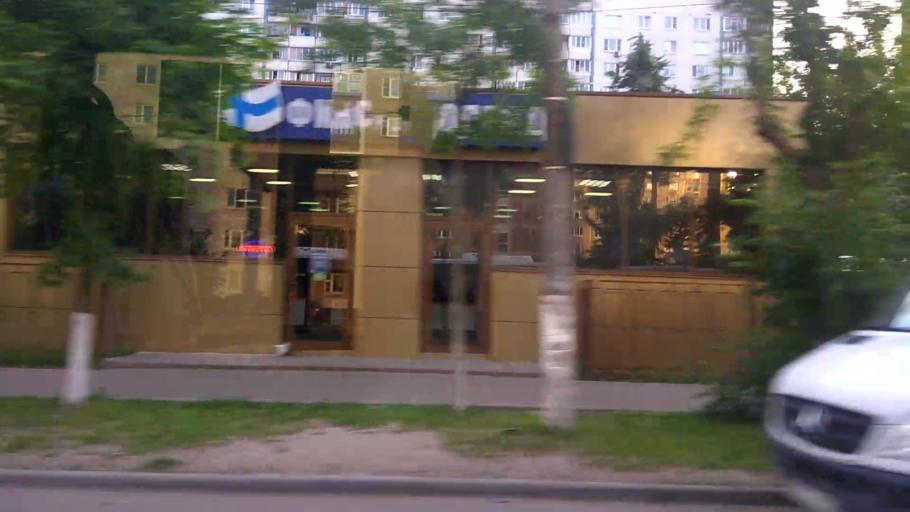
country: RU
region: Moskovskaya
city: Yubileyny
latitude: 55.9210
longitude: 37.8684
